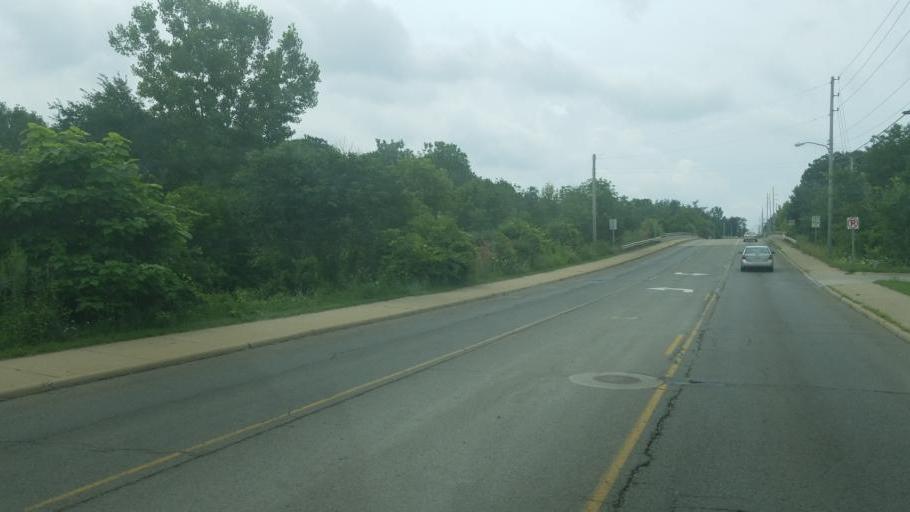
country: US
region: Ohio
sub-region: Richland County
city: Mansfield
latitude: 40.7632
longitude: -82.5517
